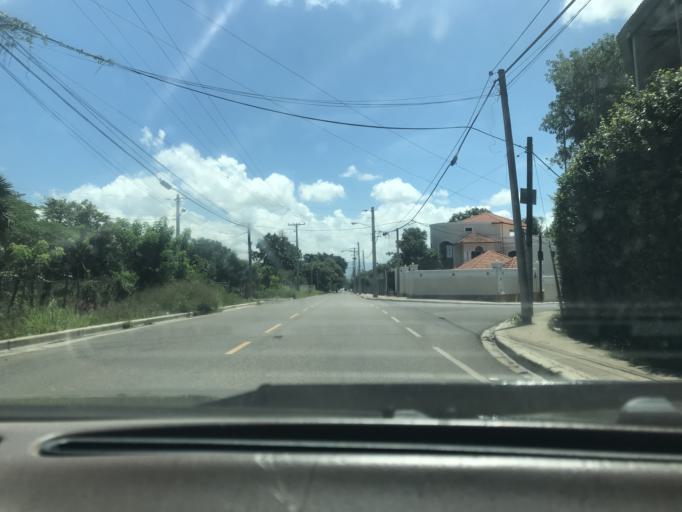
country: DO
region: Santiago
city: Santiago de los Caballeros
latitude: 19.4023
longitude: -70.7257
